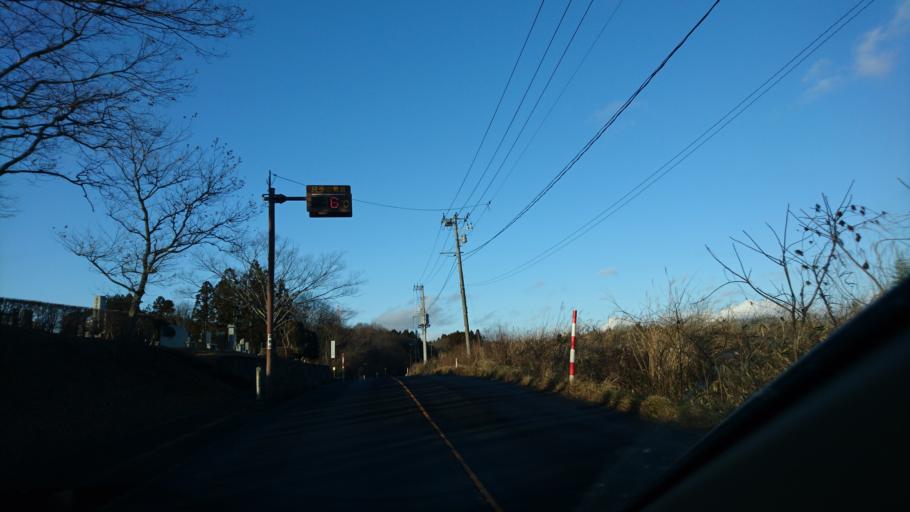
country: JP
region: Miyagi
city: Furukawa
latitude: 38.6095
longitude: 140.8708
